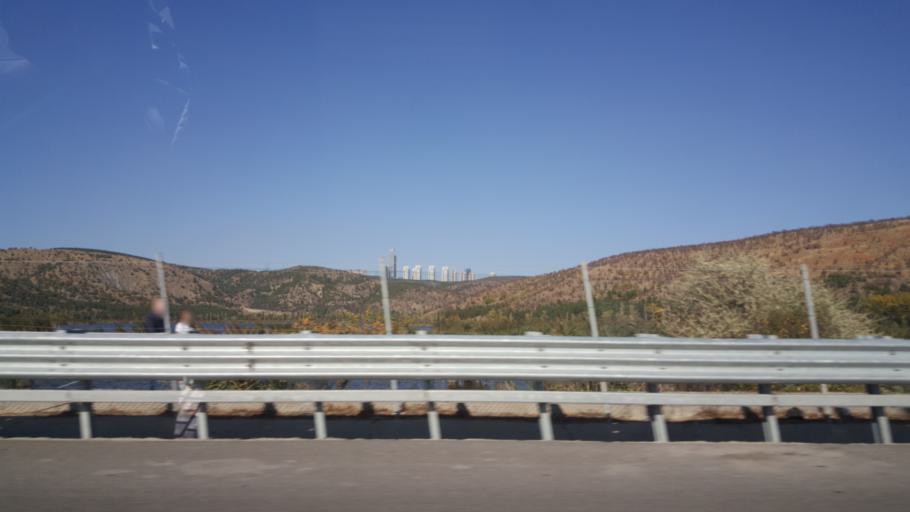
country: TR
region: Ankara
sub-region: Goelbasi
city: Golbasi
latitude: 39.8135
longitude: 32.8181
